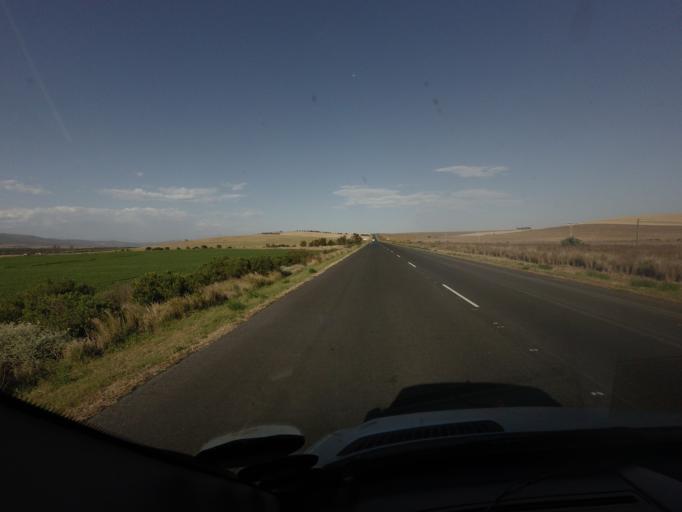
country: ZA
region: Western Cape
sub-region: Cape Winelands District Municipality
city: Ashton
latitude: -34.1422
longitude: 19.9989
